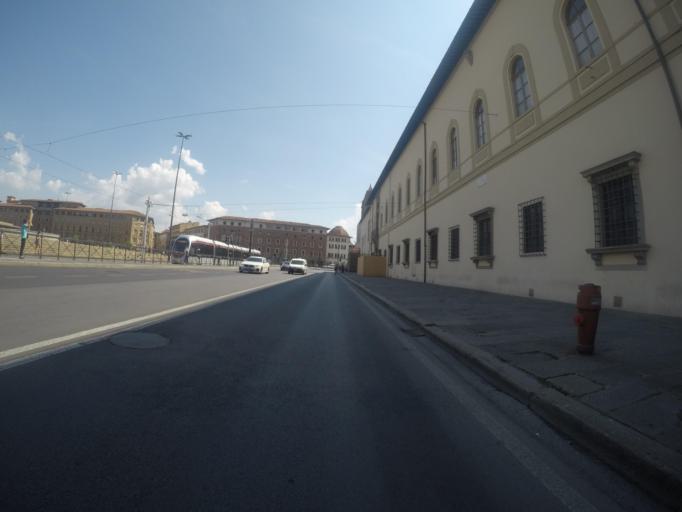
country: IT
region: Tuscany
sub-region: Province of Florence
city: Florence
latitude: 43.7753
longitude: 11.2480
